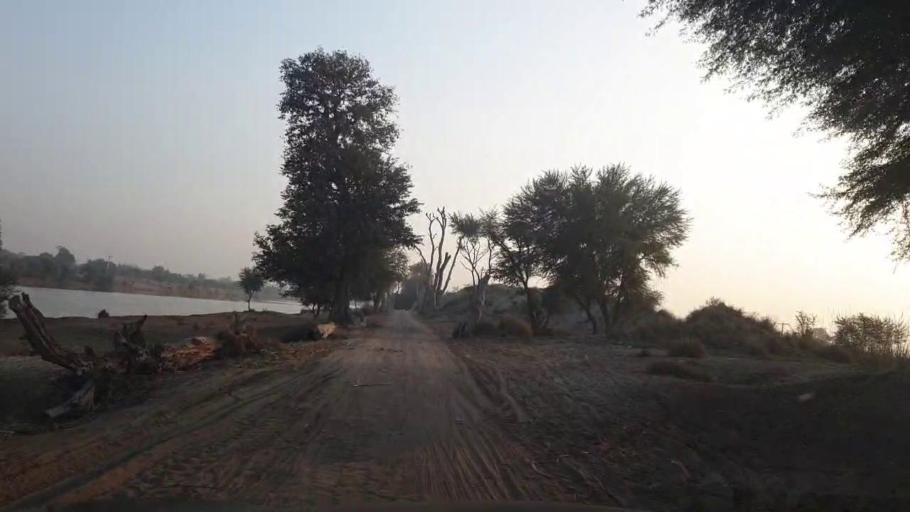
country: PK
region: Sindh
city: Ubauro
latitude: 28.3075
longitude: 69.7898
